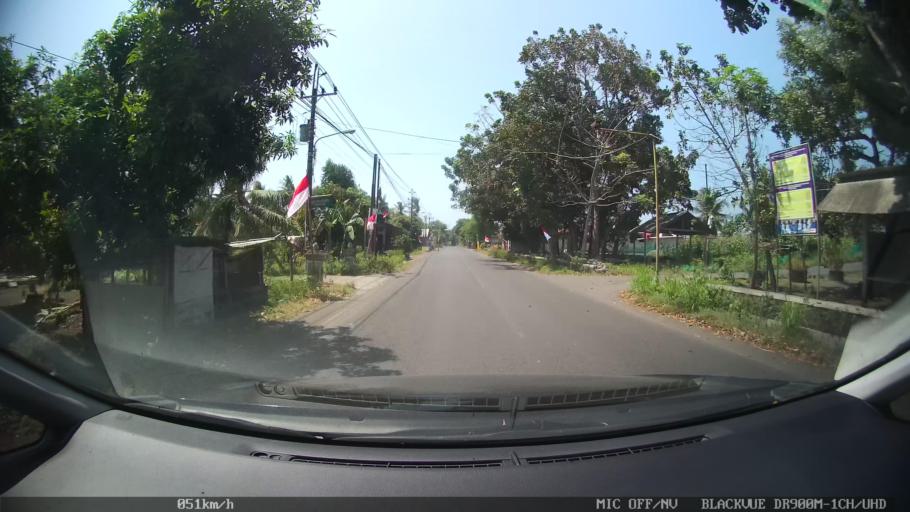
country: ID
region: Daerah Istimewa Yogyakarta
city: Srandakan
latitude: -7.9108
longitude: 110.0883
